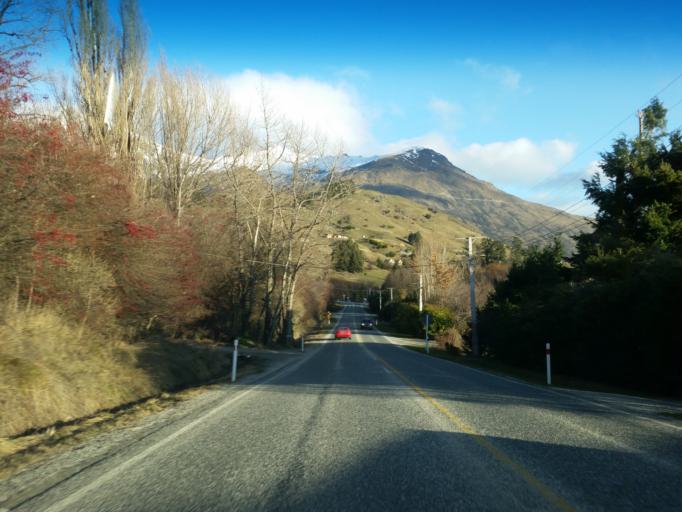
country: NZ
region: Otago
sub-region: Queenstown-Lakes District
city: Arrowtown
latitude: -44.9843
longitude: 168.8159
